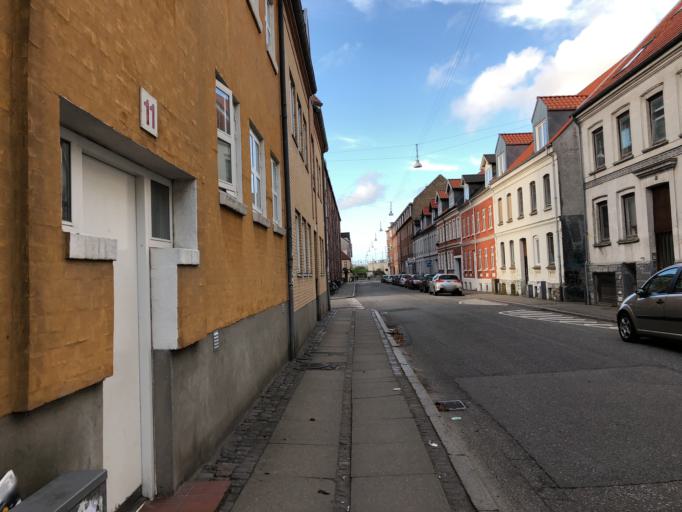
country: DK
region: North Denmark
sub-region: Alborg Kommune
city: Aalborg
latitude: 57.0511
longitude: 9.9076
